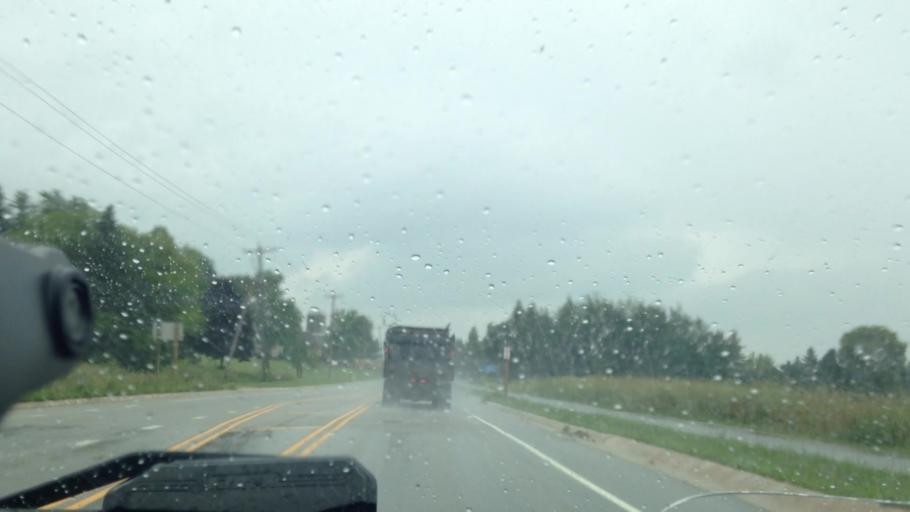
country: US
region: Wisconsin
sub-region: Washington County
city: Richfield
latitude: 43.2431
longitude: -88.1893
